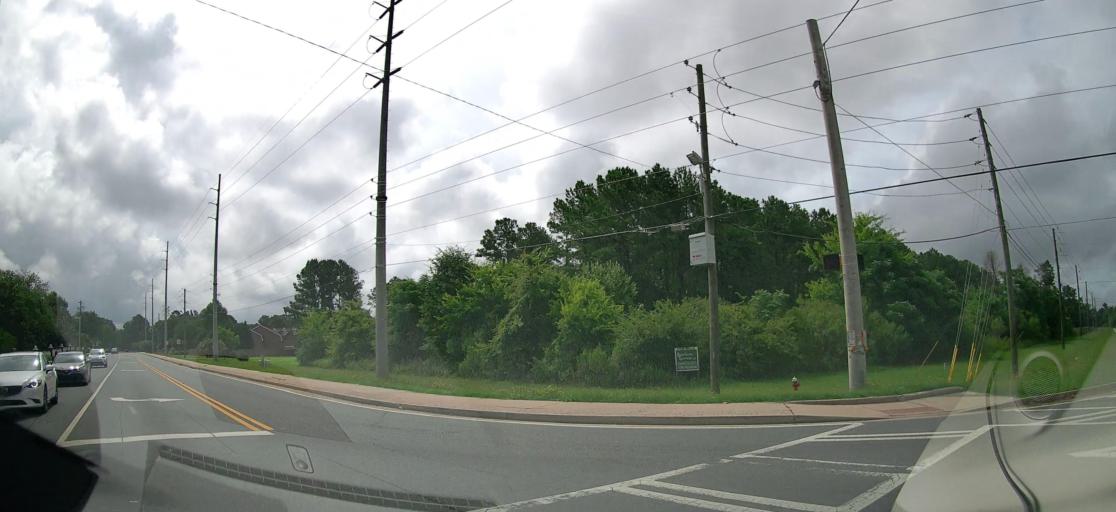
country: US
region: Georgia
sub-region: Houston County
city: Centerville
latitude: 32.6214
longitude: -83.7082
